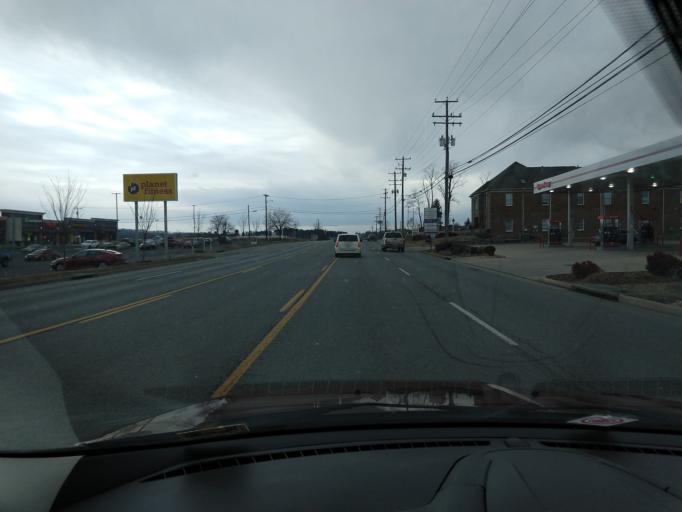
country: US
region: Virginia
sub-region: City of Waynesboro
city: Waynesboro
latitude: 38.0797
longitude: -78.9228
